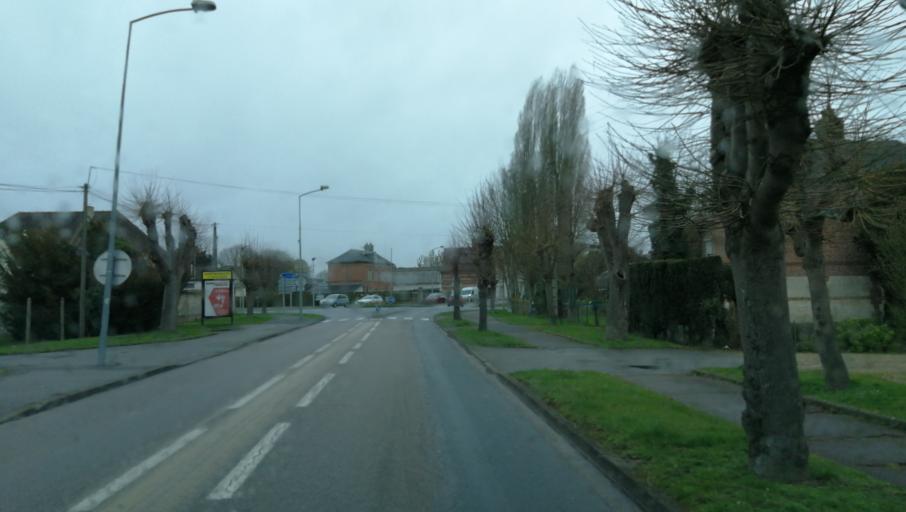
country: FR
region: Haute-Normandie
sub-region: Departement de l'Eure
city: Brionne
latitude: 49.1924
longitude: 0.7211
